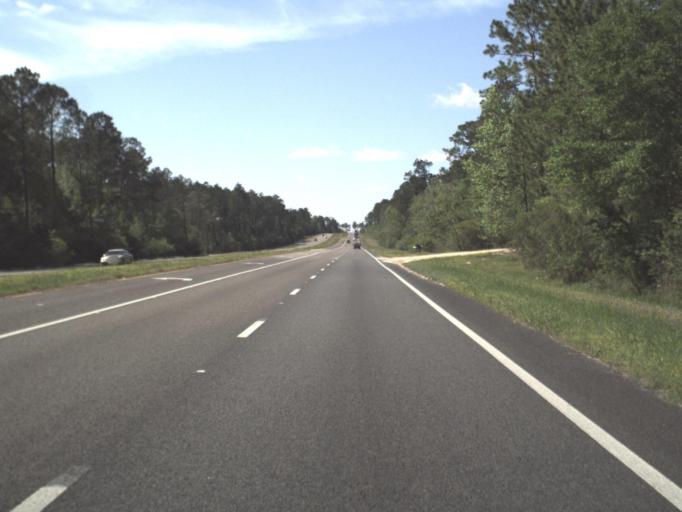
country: US
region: Florida
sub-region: Escambia County
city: Cantonment
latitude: 30.6416
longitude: -87.3436
